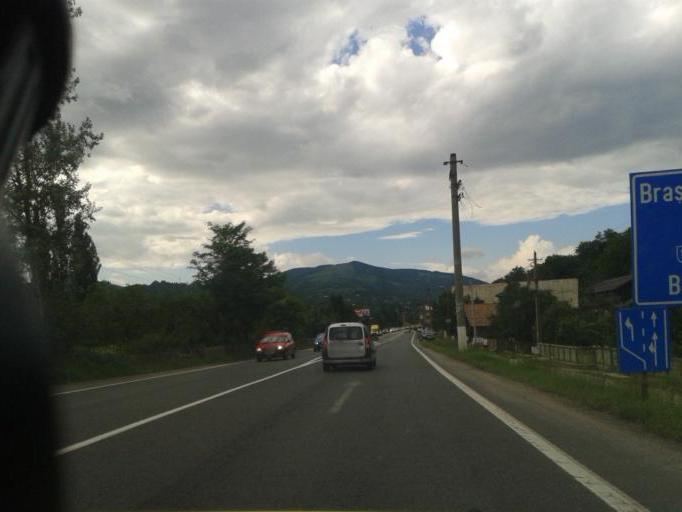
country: RO
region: Prahova
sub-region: Oras Breaza
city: Gura Beliei
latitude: 45.2244
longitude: 25.6417
